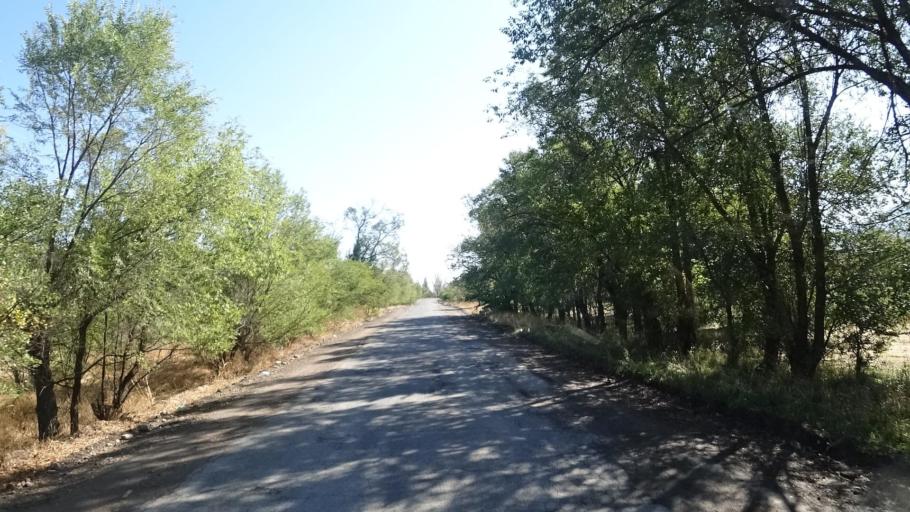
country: KG
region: Chuy
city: Bishkek
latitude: 42.7369
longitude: 74.5340
